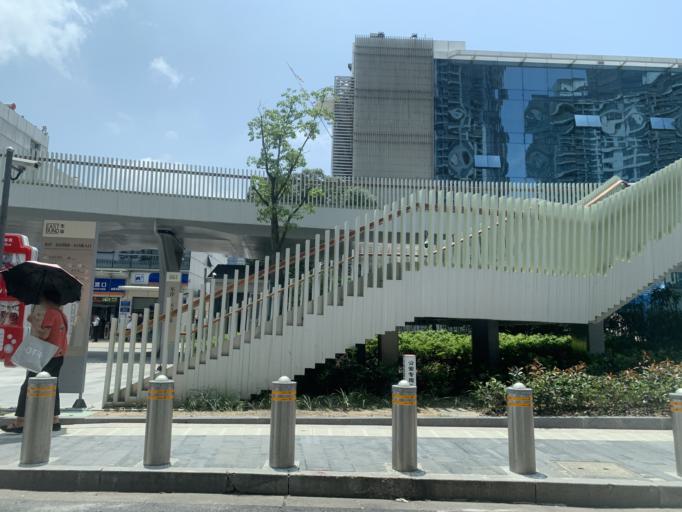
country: CN
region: Shanghai Shi
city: Hongkou
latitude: 31.2326
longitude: 121.4991
